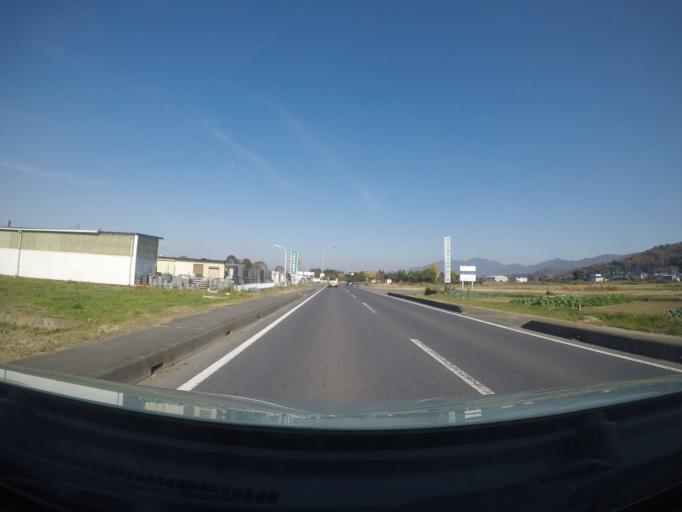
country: JP
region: Ibaraki
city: Makabe
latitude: 36.2533
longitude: 140.0738
